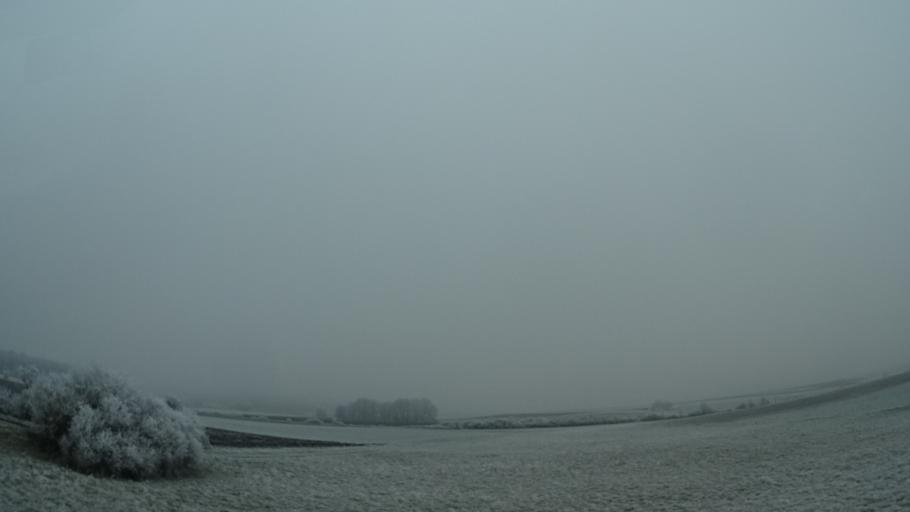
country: DE
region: Bavaria
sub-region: Regierungsbezirk Unterfranken
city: Hassfurt
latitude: 50.0665
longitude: 10.5523
